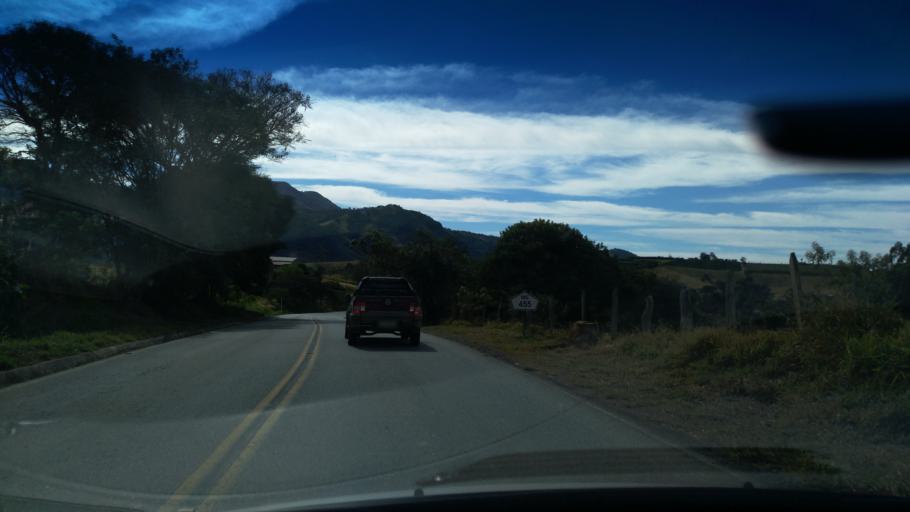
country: BR
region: Minas Gerais
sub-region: Andradas
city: Andradas
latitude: -22.0685
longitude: -46.4413
